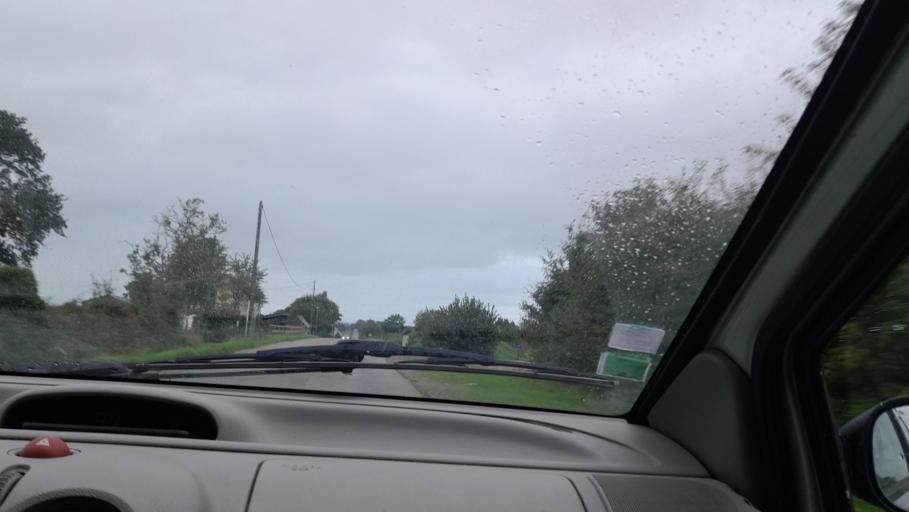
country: FR
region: Pays de la Loire
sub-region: Departement de la Mayenne
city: Ballots
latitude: 47.9107
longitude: -1.1013
